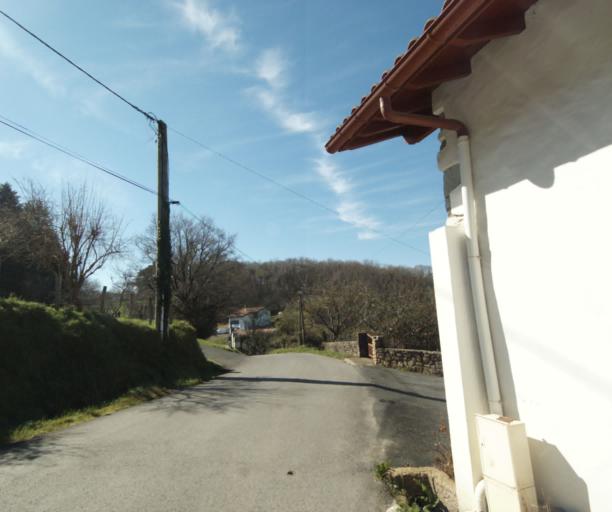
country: FR
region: Aquitaine
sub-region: Departement des Pyrenees-Atlantiques
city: Ciboure
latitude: 43.3660
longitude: -1.6771
